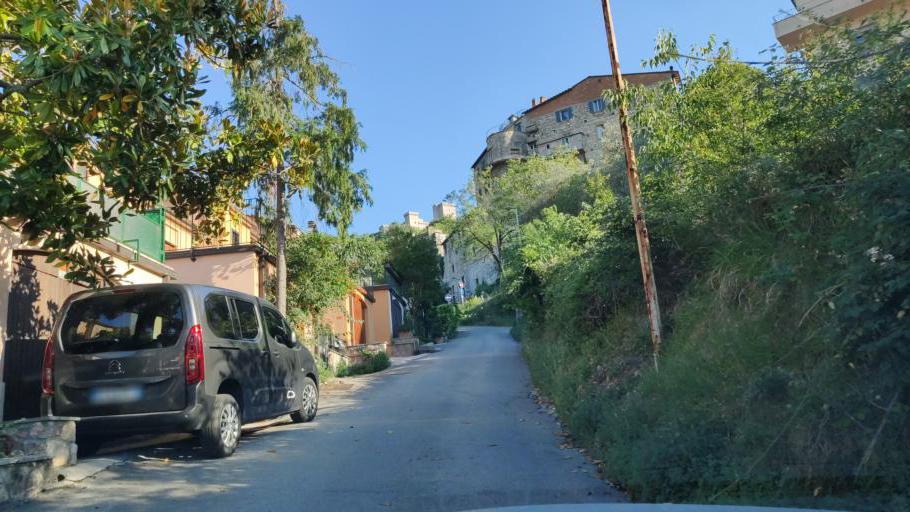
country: IT
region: Umbria
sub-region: Provincia di Terni
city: Narni
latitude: 42.5187
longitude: 12.5199
